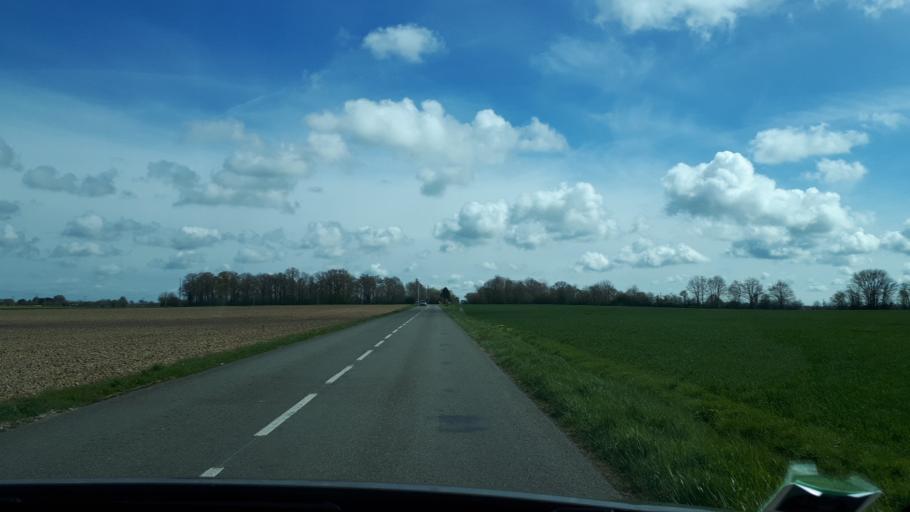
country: FR
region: Pays de la Loire
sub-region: Departement de la Sarthe
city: Bouloire
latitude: 47.8984
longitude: 0.5917
